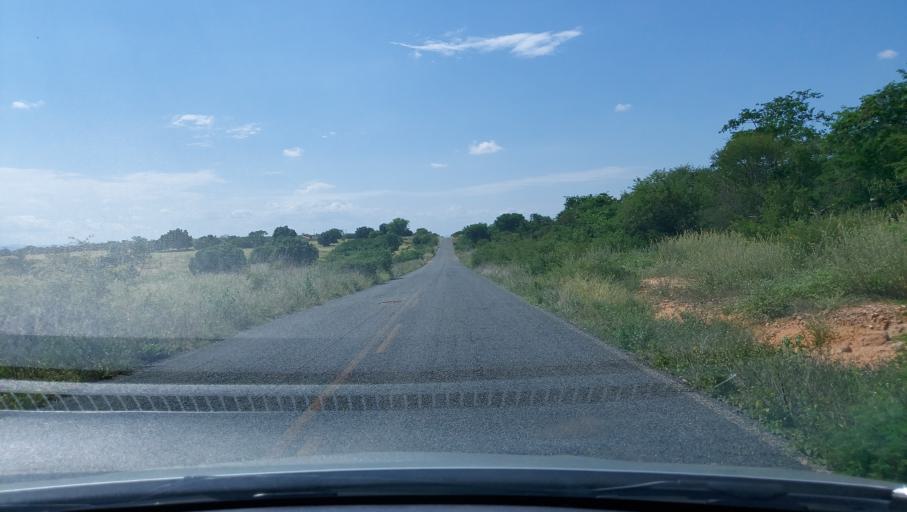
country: BR
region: Bahia
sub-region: Oliveira Dos Brejinhos
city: Beira Rio
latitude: -12.1585
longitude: -42.5504
